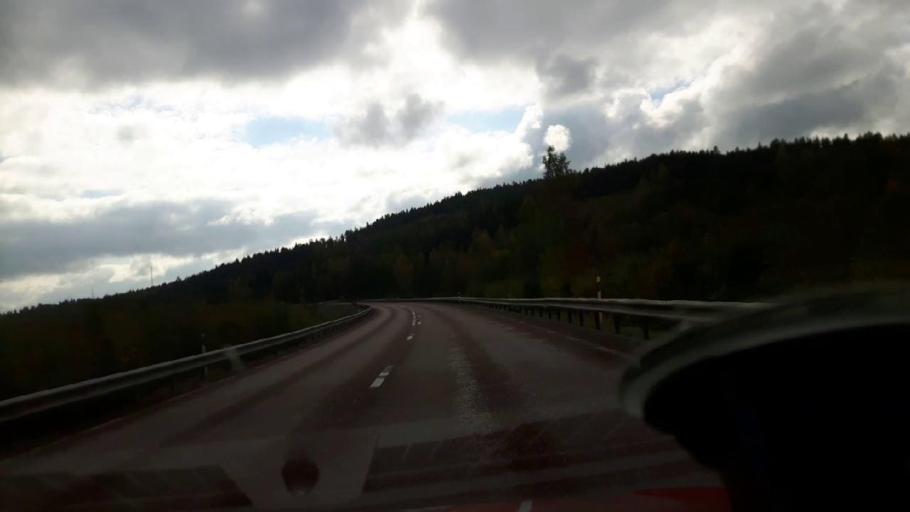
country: SE
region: Gaevleborg
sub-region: Bollnas Kommun
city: Arbra
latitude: 61.5979
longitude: 16.2964
